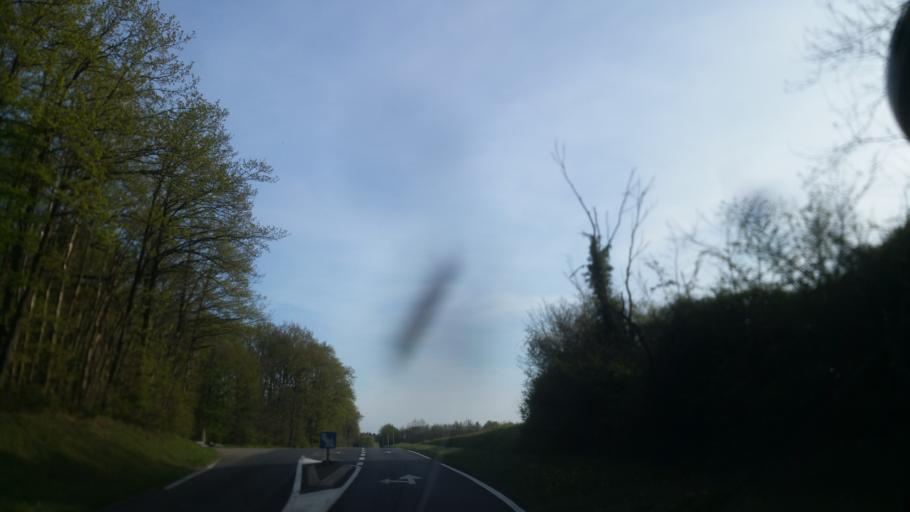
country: FR
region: Ile-de-France
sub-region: Departement de l'Essonne
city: Saint-Cyr-sous-Dourdan
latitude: 48.5496
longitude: 2.0214
